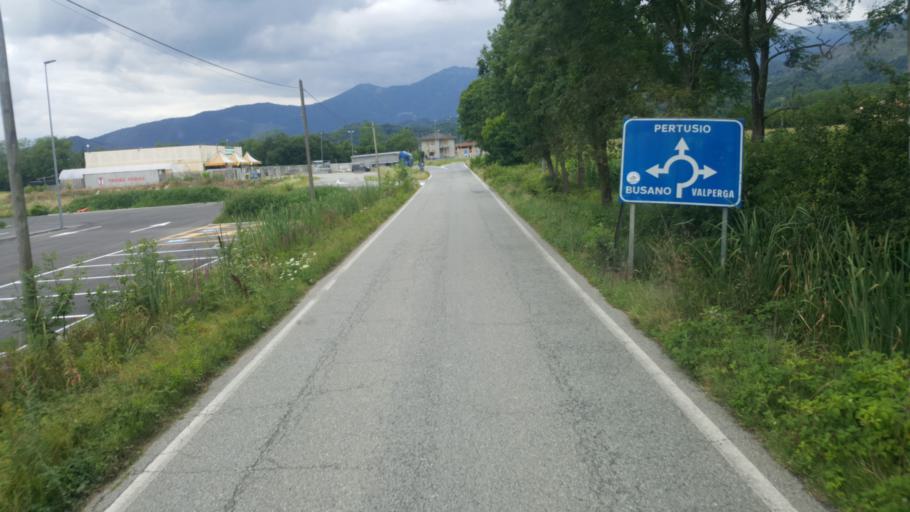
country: IT
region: Piedmont
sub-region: Provincia di Torino
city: San Ponso
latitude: 45.3523
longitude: 7.6607
